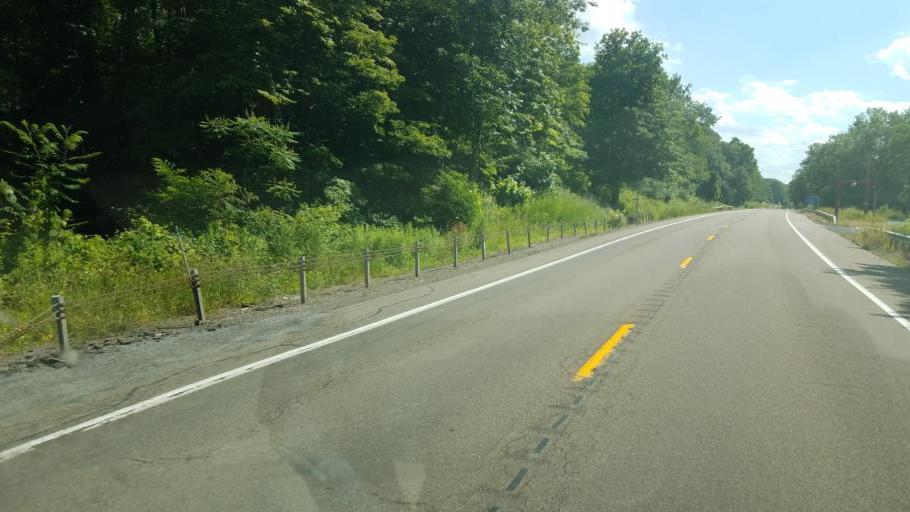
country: US
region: New York
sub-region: Steuben County
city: Sylvan Beach
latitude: 42.5000
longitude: -77.1110
